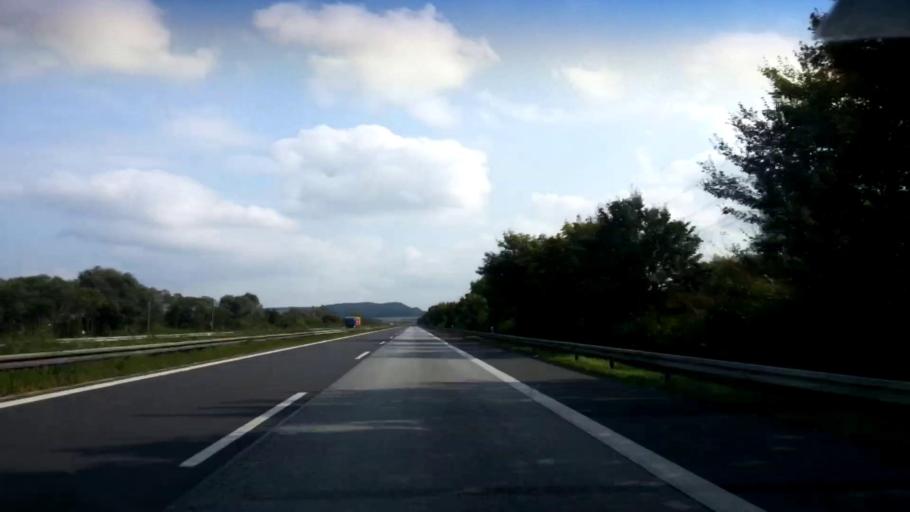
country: DE
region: Bavaria
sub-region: Regierungsbezirk Unterfranken
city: Stettfeld
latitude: 49.9714
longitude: 10.7040
